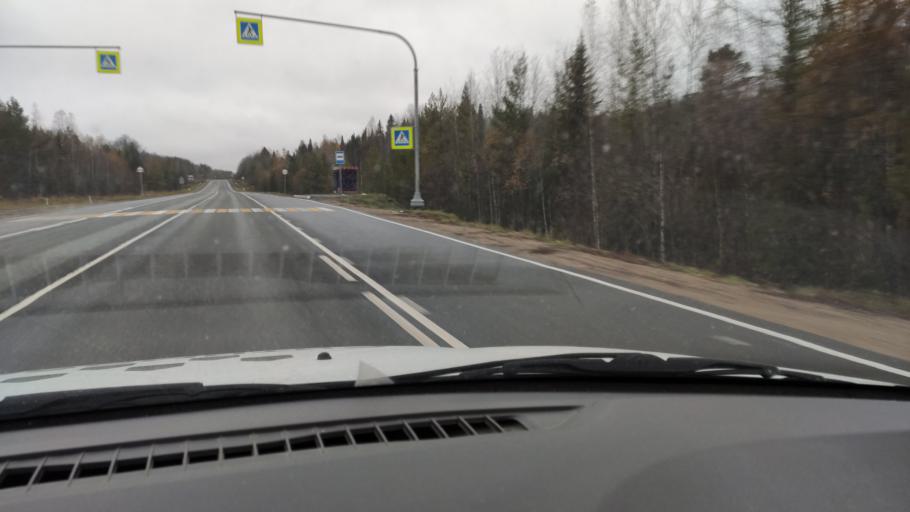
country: RU
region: Kirov
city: Omutninsk
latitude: 58.6971
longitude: 52.1238
